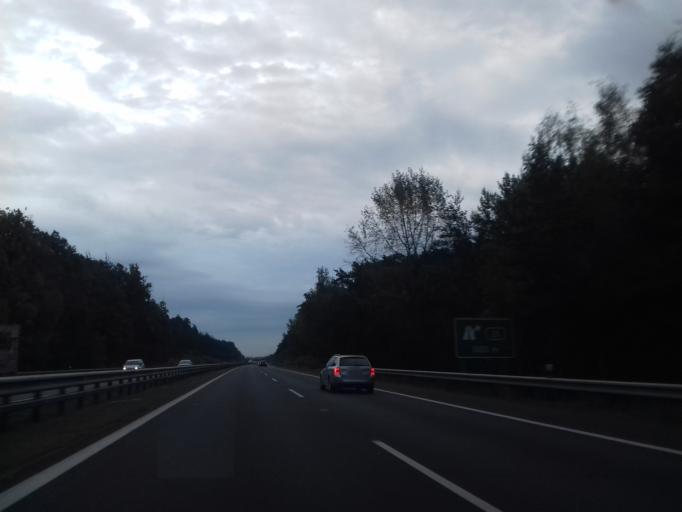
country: CZ
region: Central Bohemia
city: Poricany
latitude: 50.1239
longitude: 14.9258
